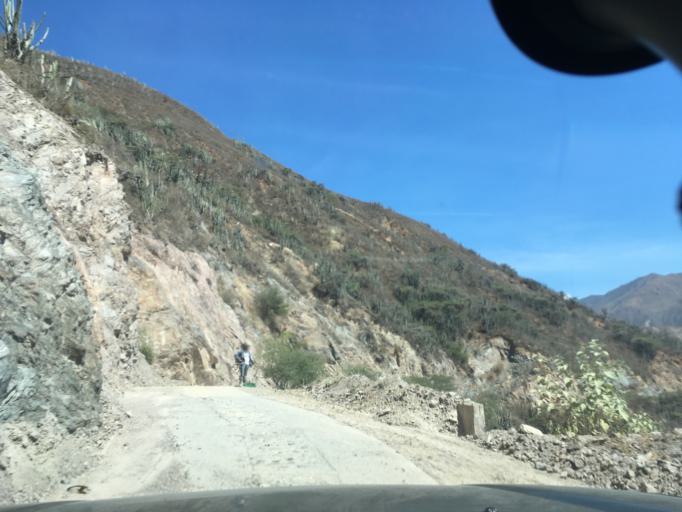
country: CO
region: Santander
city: Aratoca
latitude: 6.7662
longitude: -72.9837
